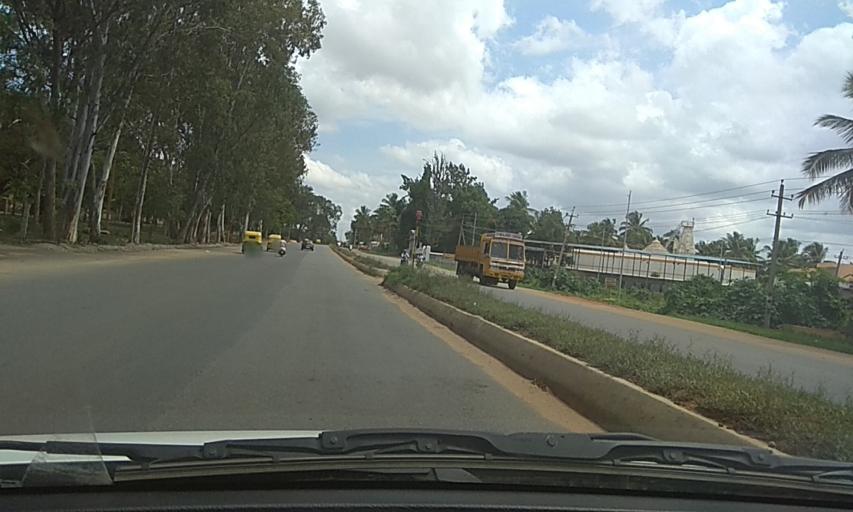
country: IN
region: Karnataka
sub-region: Tumkur
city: Tumkur
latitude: 13.3688
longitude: 77.1022
